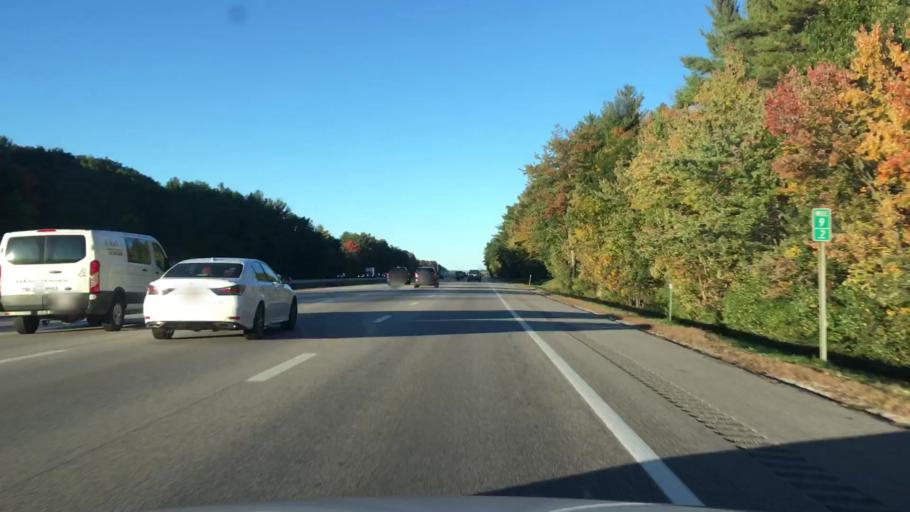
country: US
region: New Hampshire
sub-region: Rockingham County
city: Greenland
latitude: 43.0092
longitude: -70.8378
